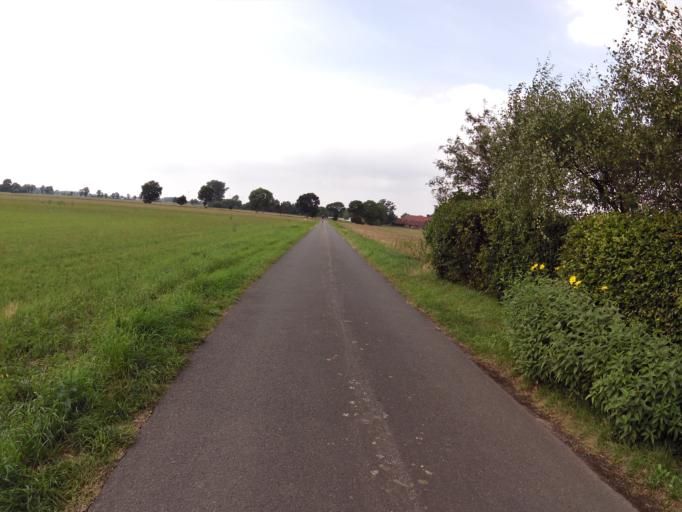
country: DE
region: Lower Saxony
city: Hilgermissen
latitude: 52.8848
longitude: 9.1757
